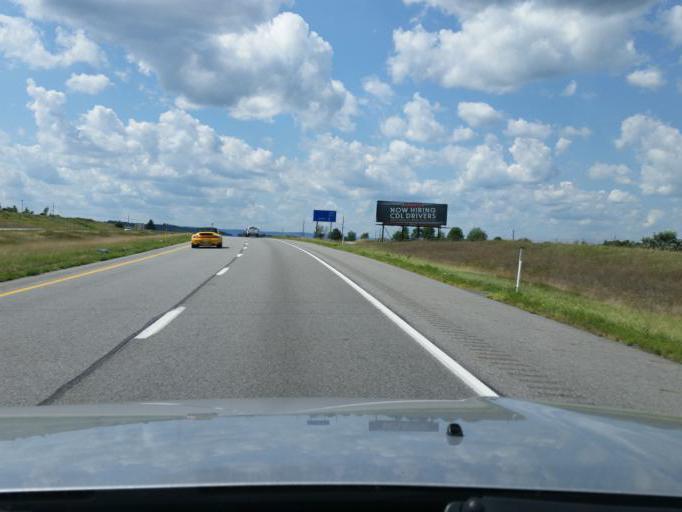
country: US
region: Pennsylvania
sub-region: Bedford County
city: Bedford
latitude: 40.0717
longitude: -78.5196
